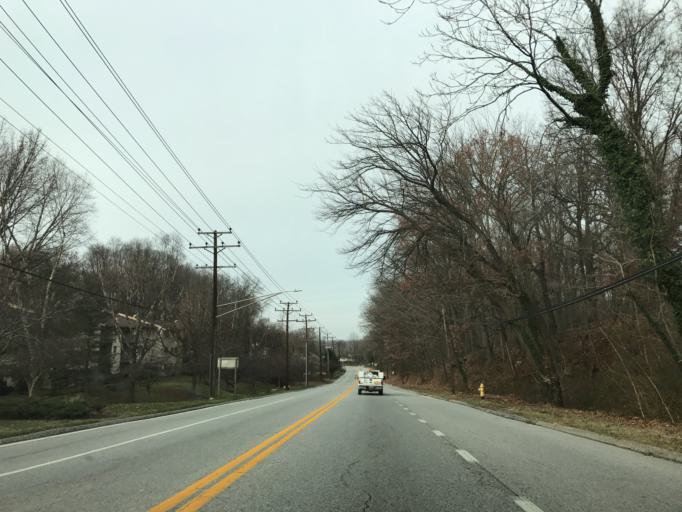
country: US
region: Maryland
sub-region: Anne Arundel County
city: Pumphrey
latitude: 39.2103
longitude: -76.6423
